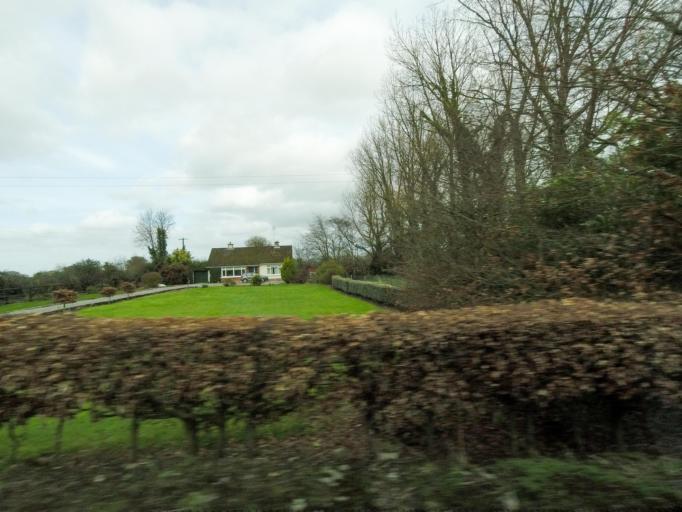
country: IE
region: Leinster
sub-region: Kildare
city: Naas
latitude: 53.1952
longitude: -6.6522
